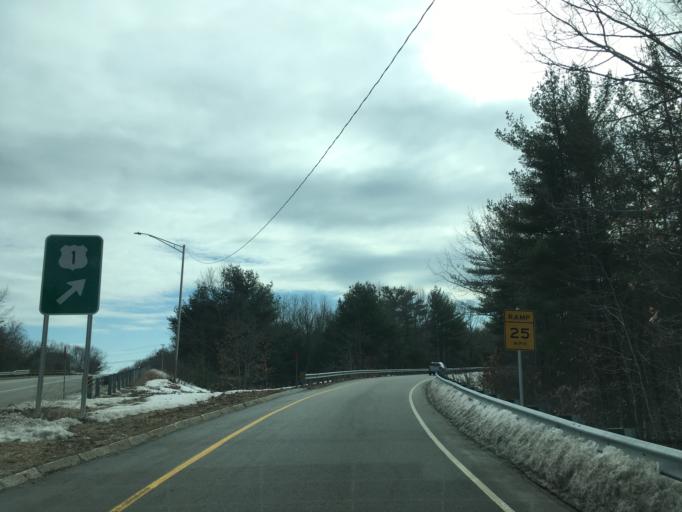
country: US
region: New Hampshire
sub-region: Rockingham County
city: Hampton
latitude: 42.9339
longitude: -70.8429
